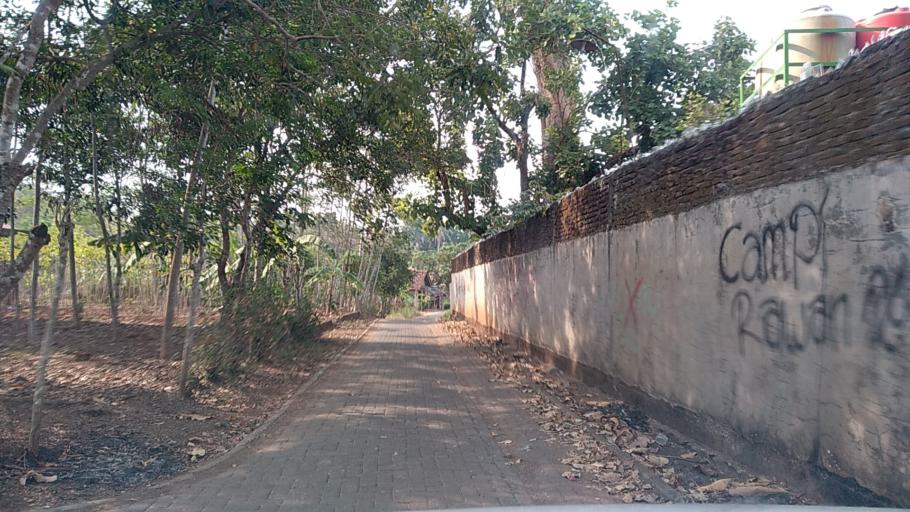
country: ID
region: Central Java
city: Semarang
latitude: -7.0505
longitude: 110.3108
